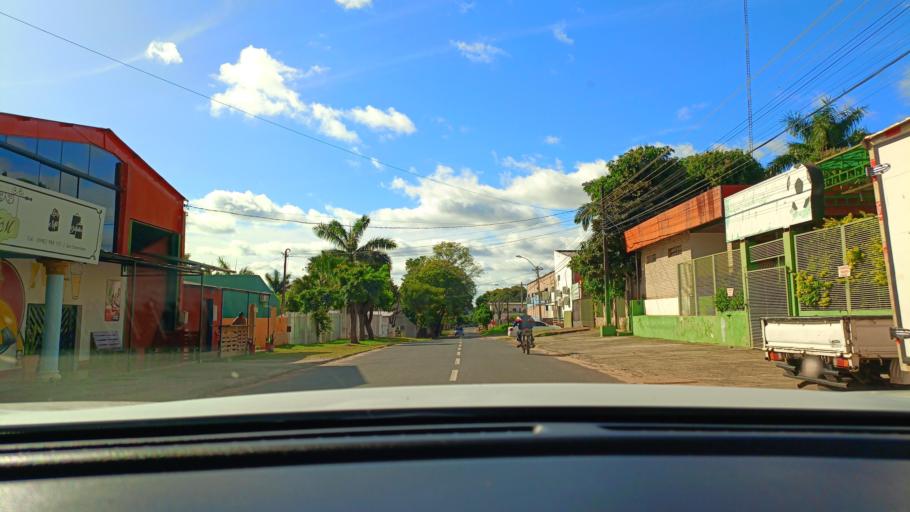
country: PY
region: San Pedro
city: Guayaybi
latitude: -24.6723
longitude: -56.4470
